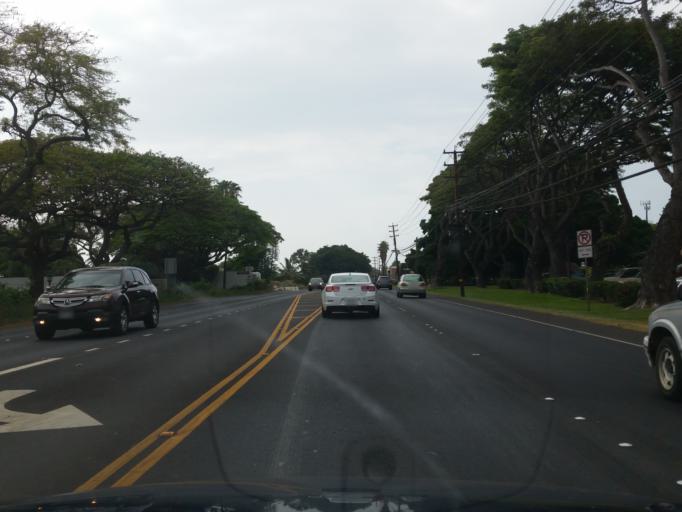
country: US
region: Hawaii
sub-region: Maui County
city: Lahaina
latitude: 20.8791
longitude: -156.6785
